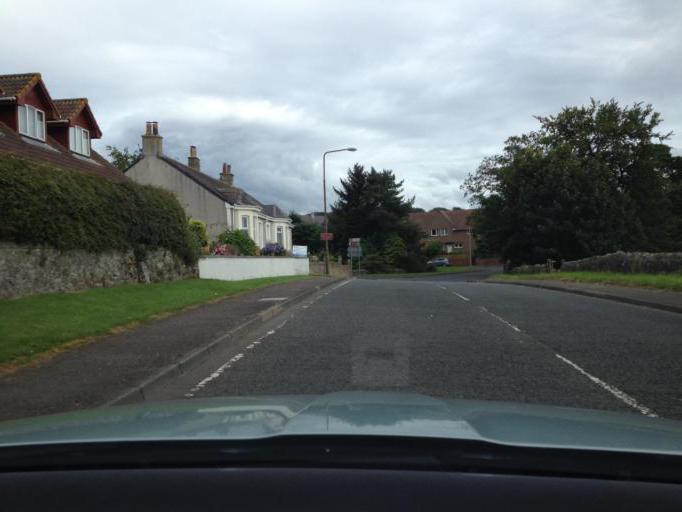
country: GB
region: Scotland
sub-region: West Lothian
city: Bathgate
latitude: 55.9140
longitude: -3.6410
